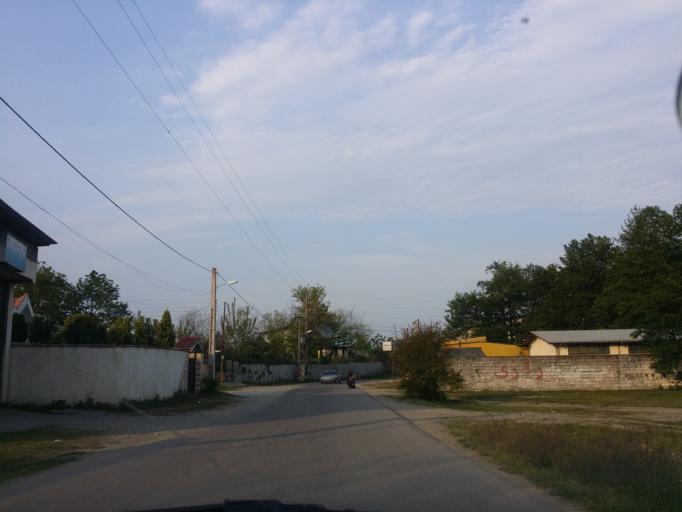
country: IR
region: Mazandaran
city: Chalus
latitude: 36.6640
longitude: 51.3771
